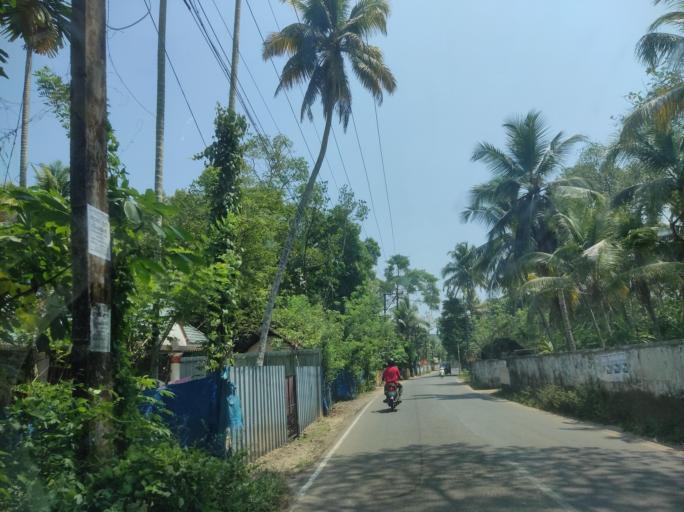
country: IN
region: Kerala
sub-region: Alappuzha
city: Kutiatodu
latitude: 9.7829
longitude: 76.3044
